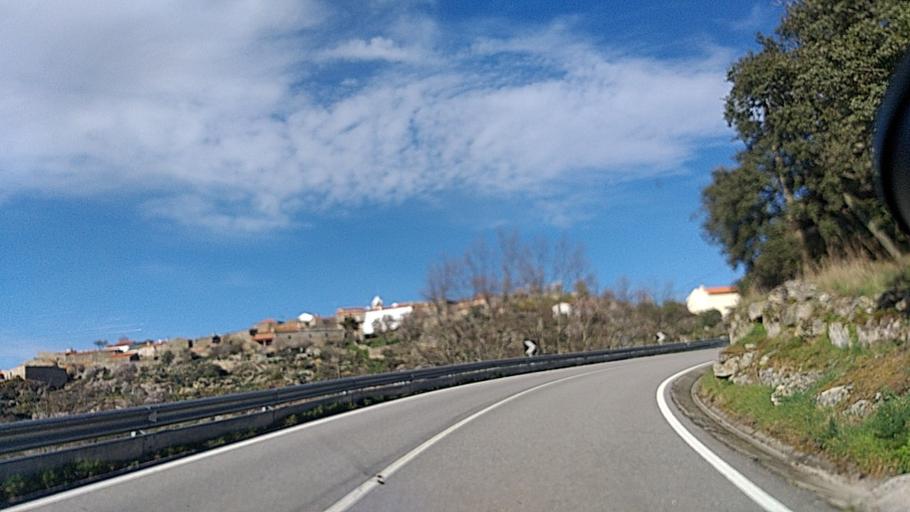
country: ES
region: Castille and Leon
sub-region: Provincia de Salamanca
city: Fuentes de Onoro
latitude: 40.6186
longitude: -6.9020
